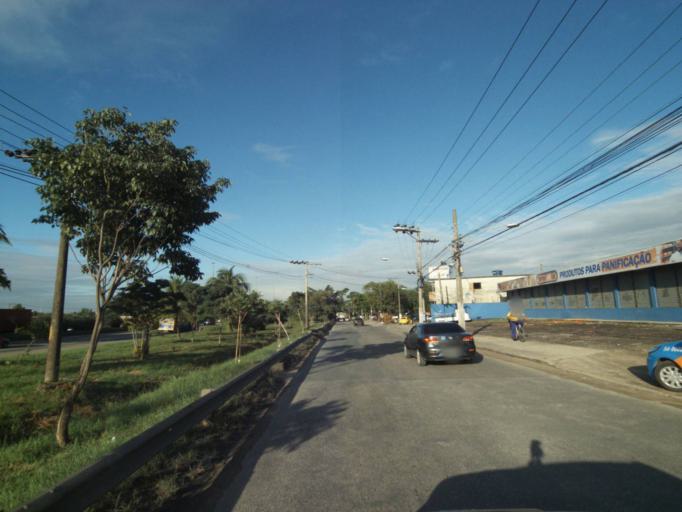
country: BR
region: Rio de Janeiro
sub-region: Nilopolis
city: Nilopolis
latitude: -22.8573
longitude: -43.4737
